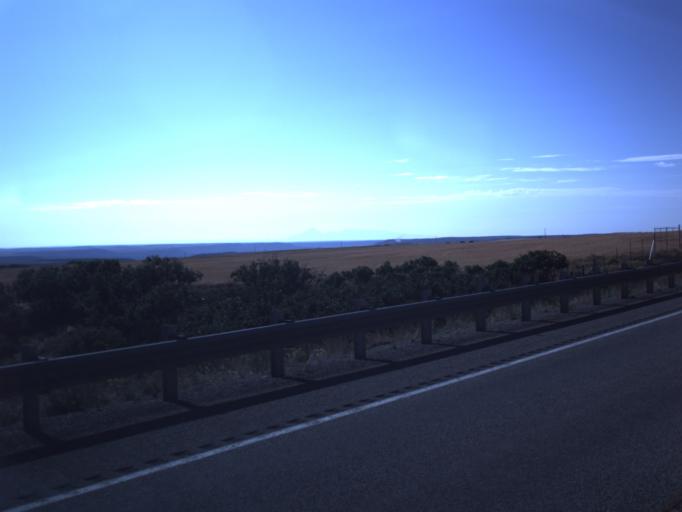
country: US
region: Utah
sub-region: San Juan County
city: Monticello
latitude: 37.8388
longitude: -109.3369
